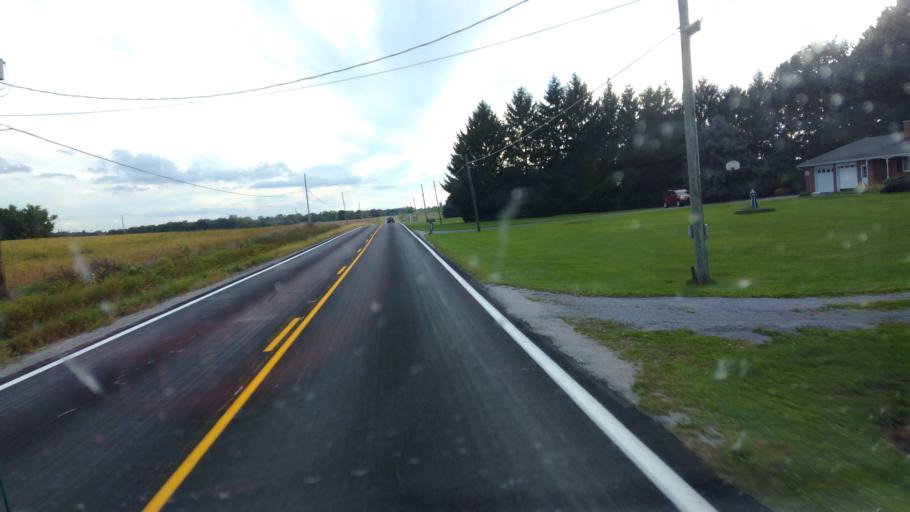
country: US
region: Ohio
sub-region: Crawford County
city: Bucyrus
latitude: 40.8439
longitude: -82.9229
